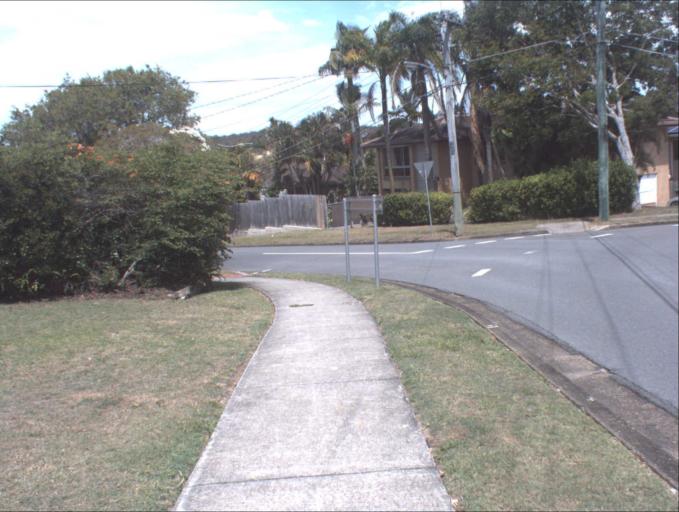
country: AU
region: Queensland
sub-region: Logan
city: Rochedale South
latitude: -27.5931
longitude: 153.1409
